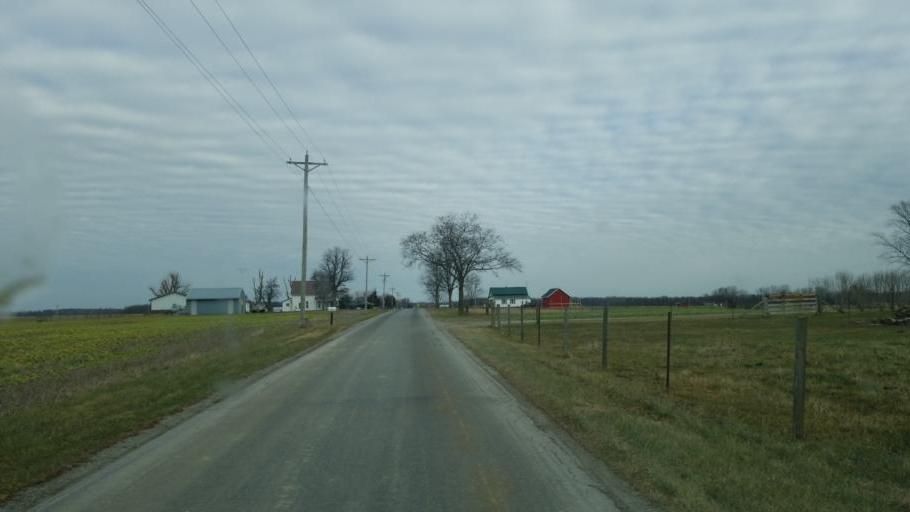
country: US
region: Ohio
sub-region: Hardin County
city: Kenton
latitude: 40.5866
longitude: -83.4522
